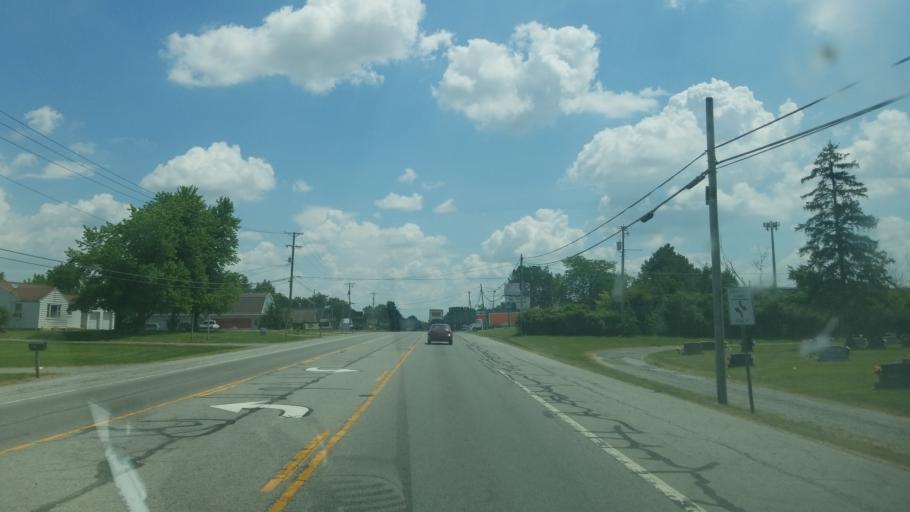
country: US
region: Ohio
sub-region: Allen County
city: Lima
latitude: 40.7309
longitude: -84.0477
